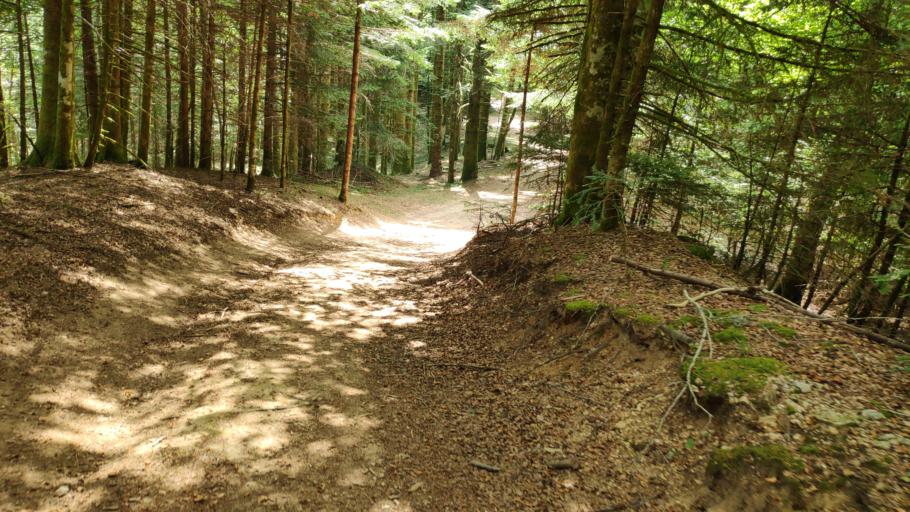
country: IT
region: Calabria
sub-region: Provincia di Vibo-Valentia
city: Serra San Bruno
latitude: 38.5423
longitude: 16.3601
